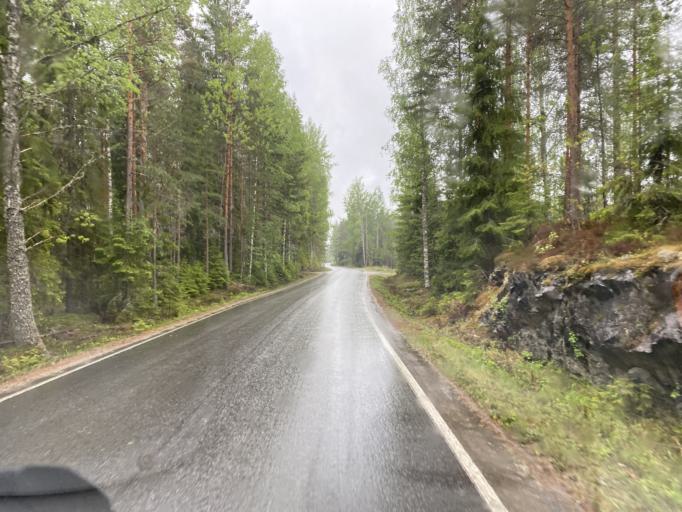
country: FI
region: Haeme
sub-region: Forssa
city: Humppila
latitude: 61.0863
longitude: 23.3095
